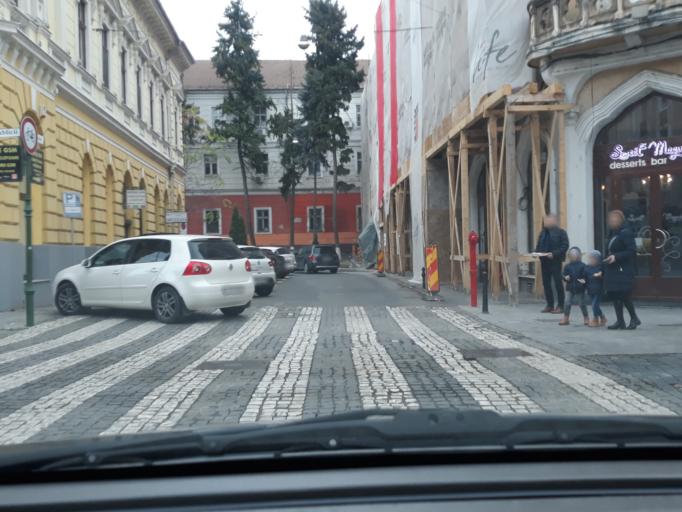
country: RO
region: Bihor
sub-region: Comuna Biharea
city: Oradea
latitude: 47.0583
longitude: 21.9336
